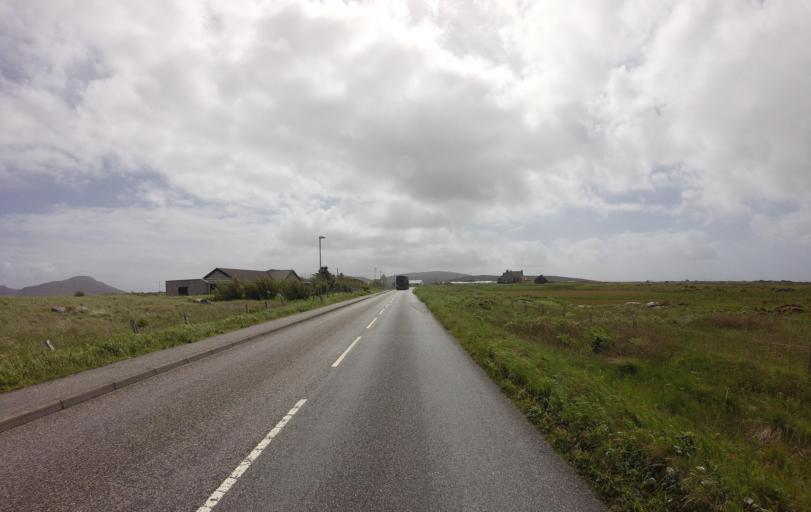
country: GB
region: Scotland
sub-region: Eilean Siar
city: Isle of South Uist
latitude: 57.1649
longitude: -7.3708
